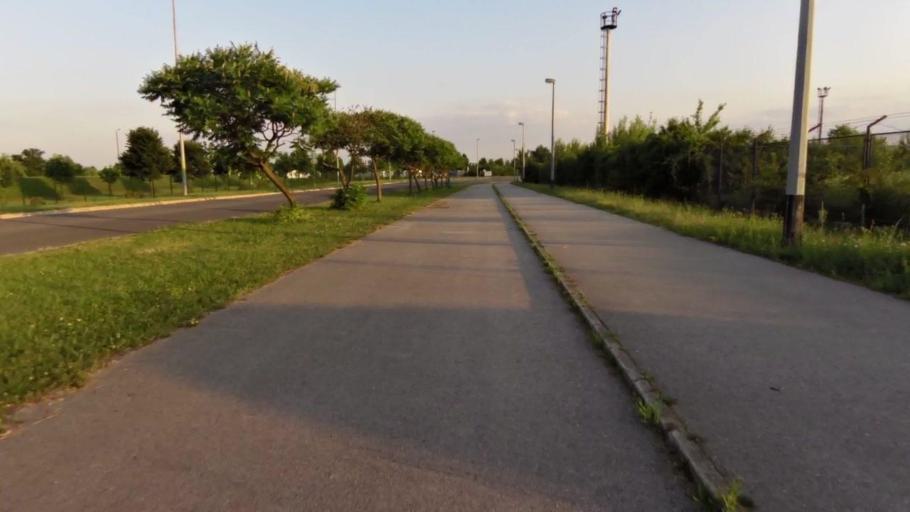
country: HR
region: Zagrebacka
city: Micevec
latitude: 45.7894
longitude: 16.0790
